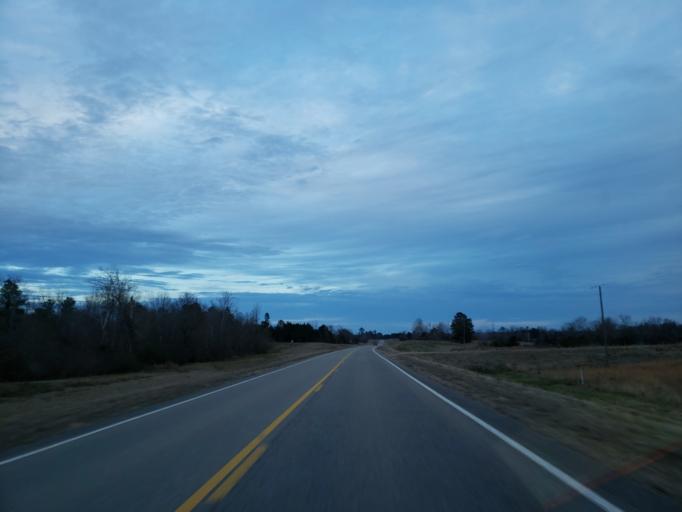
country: US
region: Mississippi
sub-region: Kemper County
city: De Kalb
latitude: 32.8307
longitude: -88.3833
